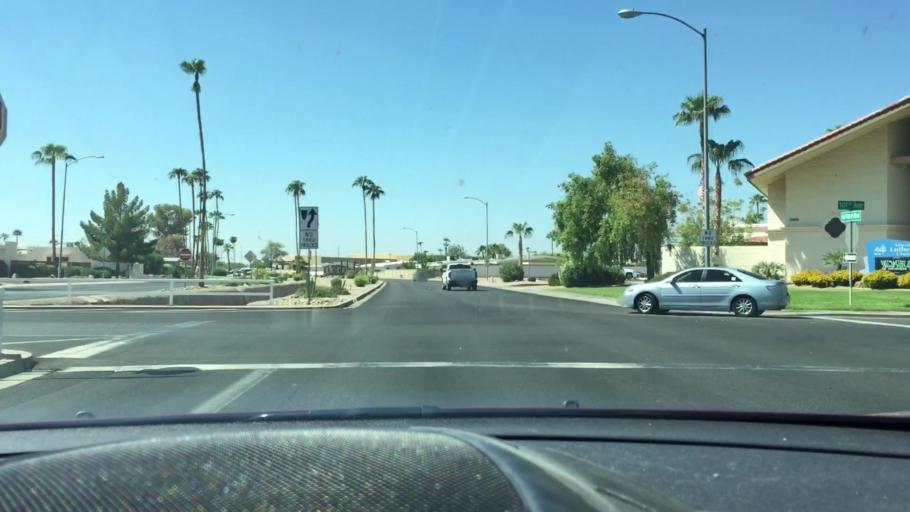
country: US
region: Arizona
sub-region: Maricopa County
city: El Mirage
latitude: 33.6415
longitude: -112.2877
